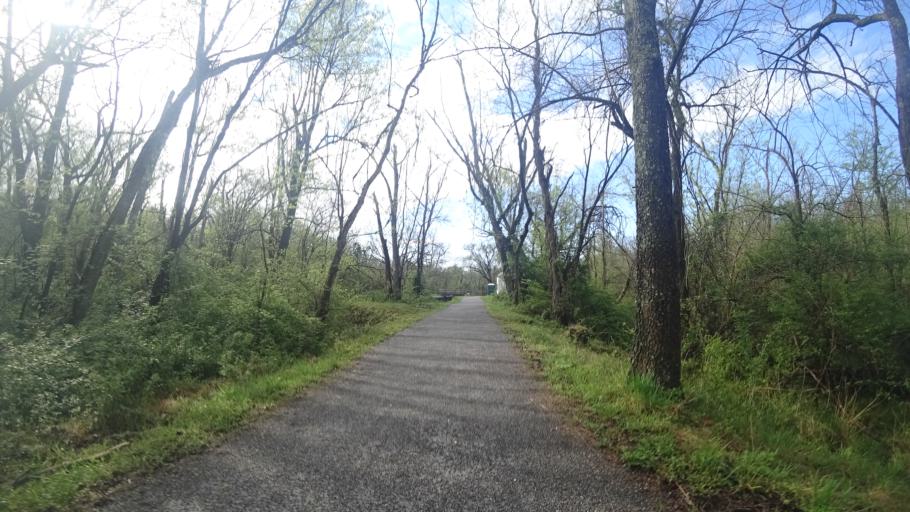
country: US
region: Virginia
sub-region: Loudoun County
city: Belmont
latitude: 39.1047
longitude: -77.4728
